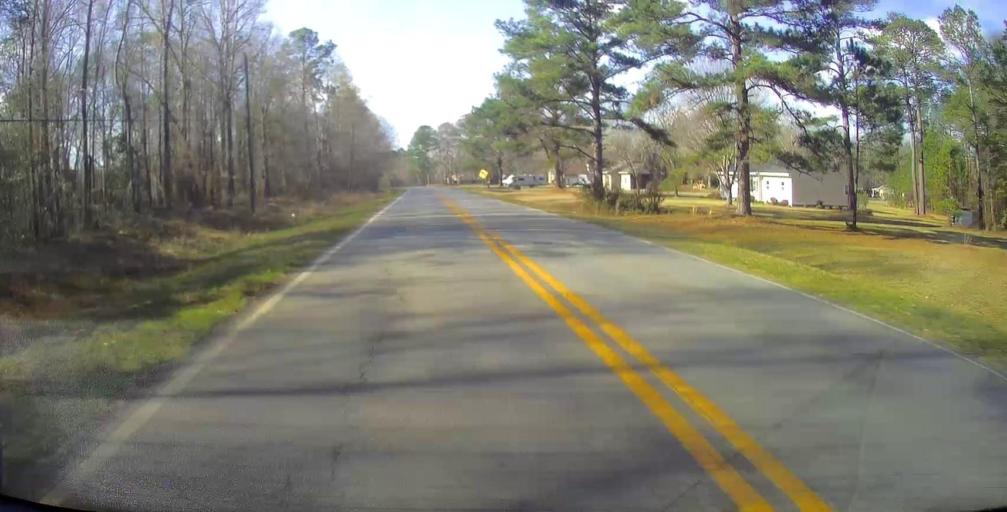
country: US
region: Georgia
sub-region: Laurens County
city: Dublin
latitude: 32.5537
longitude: -82.9944
